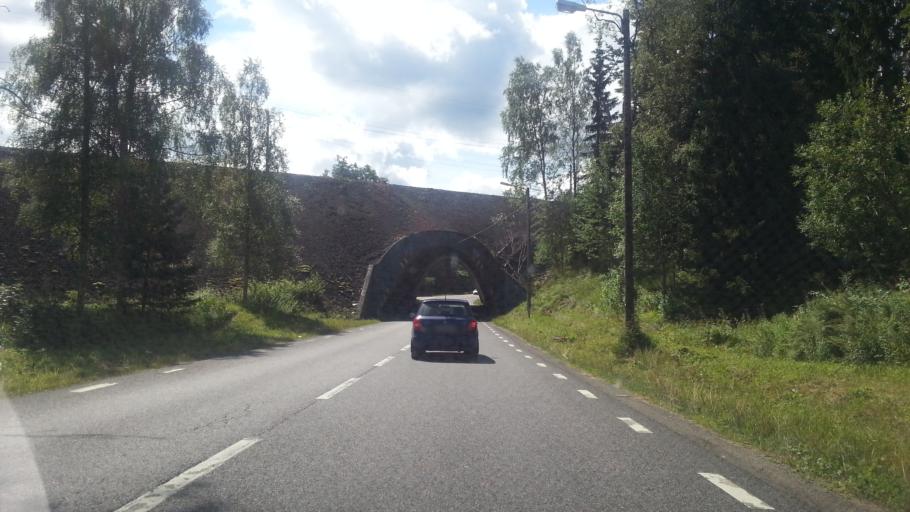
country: SE
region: Dalarna
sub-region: Ludvika Kommun
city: Grangesberg
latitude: 60.0688
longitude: 14.9869
